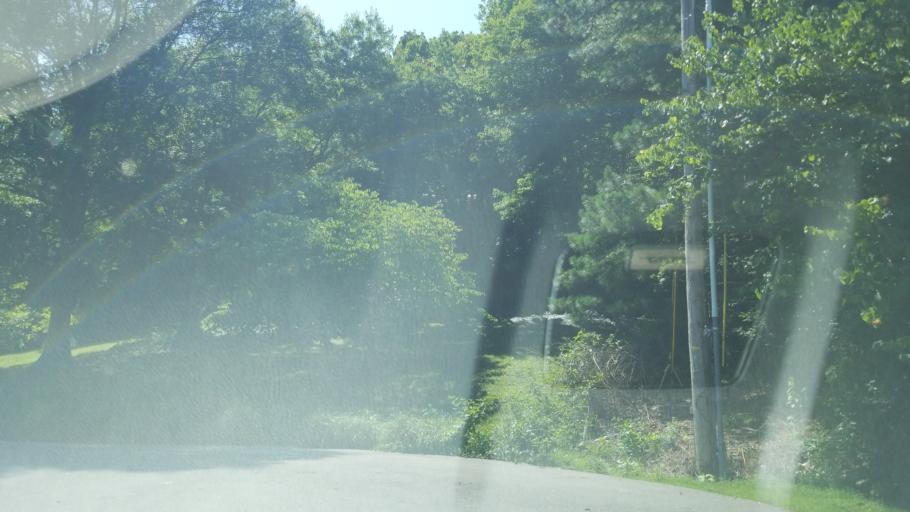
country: US
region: Tennessee
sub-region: Davidson County
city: Forest Hills
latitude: 36.0594
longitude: -86.8206
